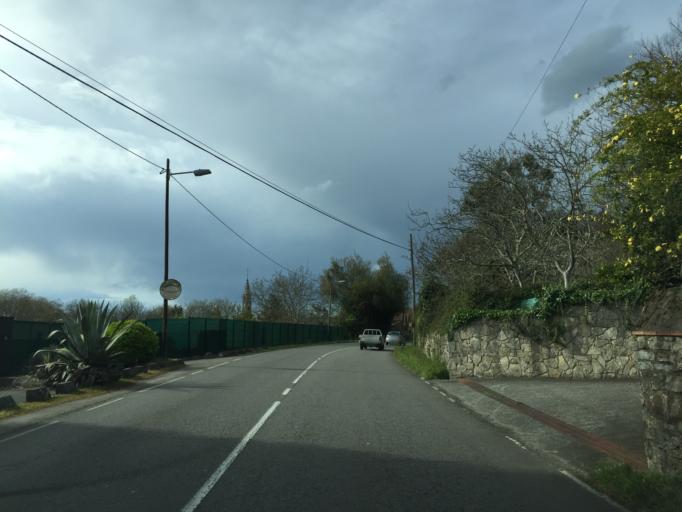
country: ES
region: Asturias
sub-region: Province of Asturias
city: Gijon
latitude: 43.5176
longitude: -5.6065
